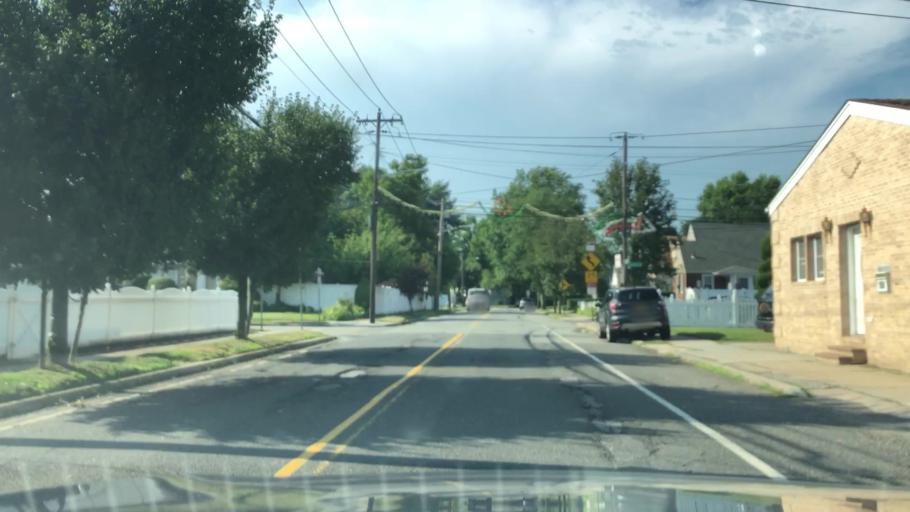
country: US
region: New York
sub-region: Nassau County
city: Franklin Square
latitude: 40.7153
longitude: -73.6776
